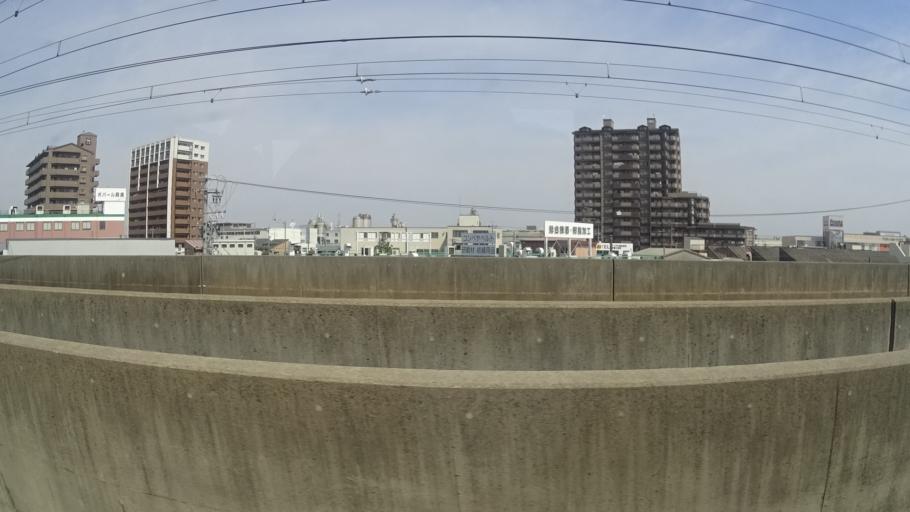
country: JP
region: Aichi
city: Kanie
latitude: 35.1473
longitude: 136.8459
